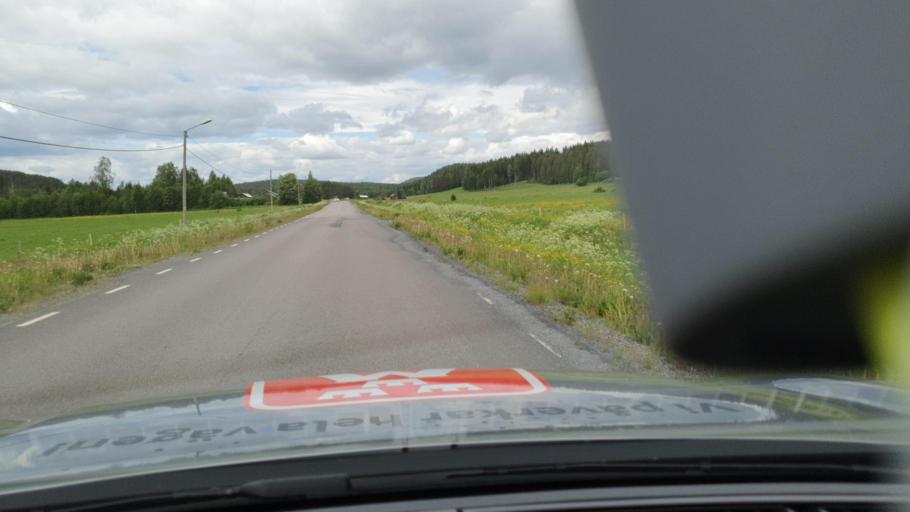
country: SE
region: Norrbotten
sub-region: Lulea Kommun
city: Sodra Sunderbyn
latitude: 65.8593
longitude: 21.9160
